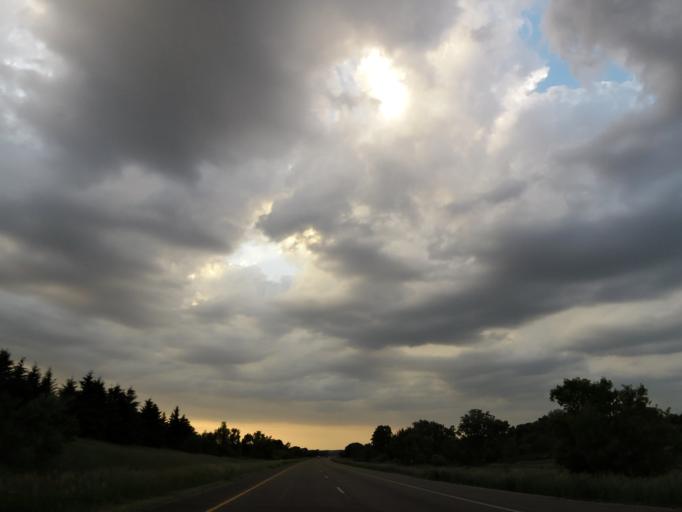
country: US
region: Wisconsin
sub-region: Eau Claire County
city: Fall Creek
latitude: 44.6950
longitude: -91.3382
